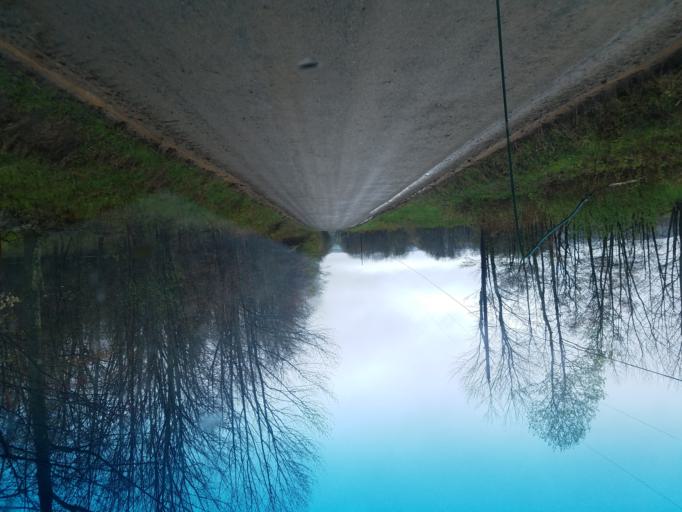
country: US
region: New York
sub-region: Allegany County
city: Andover
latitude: 41.9891
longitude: -77.7301
